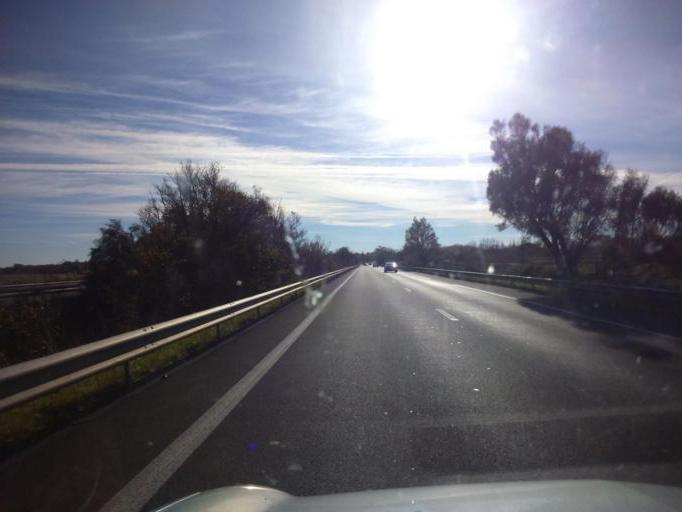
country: FR
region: Poitou-Charentes
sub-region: Departement de la Charente-Maritime
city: Breuil-Magne
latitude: 45.9760
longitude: -0.9929
